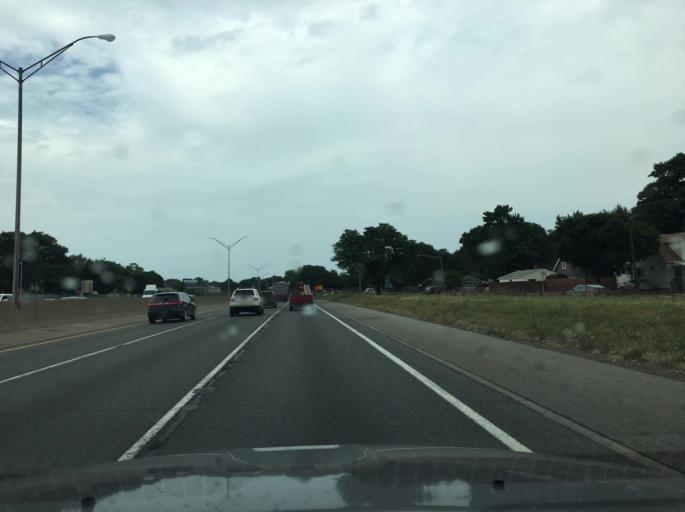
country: US
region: Michigan
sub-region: Oakland County
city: Hazel Park
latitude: 42.4514
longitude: -83.0949
